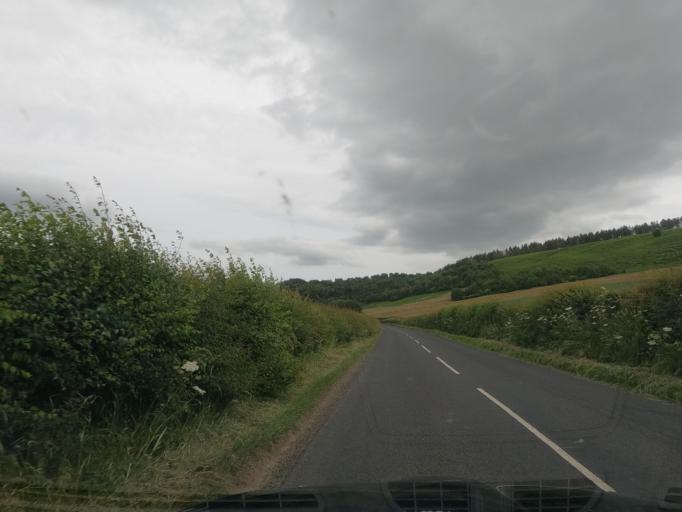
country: GB
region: England
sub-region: Northumberland
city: Doddington
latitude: 55.5560
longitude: -1.9810
